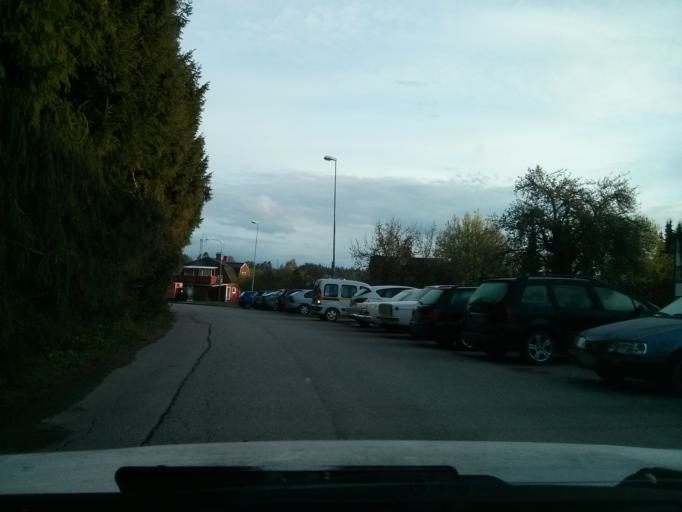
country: SE
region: Soedermanland
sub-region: Nykopings Kommun
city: Nykoping
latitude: 58.7763
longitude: 16.9824
